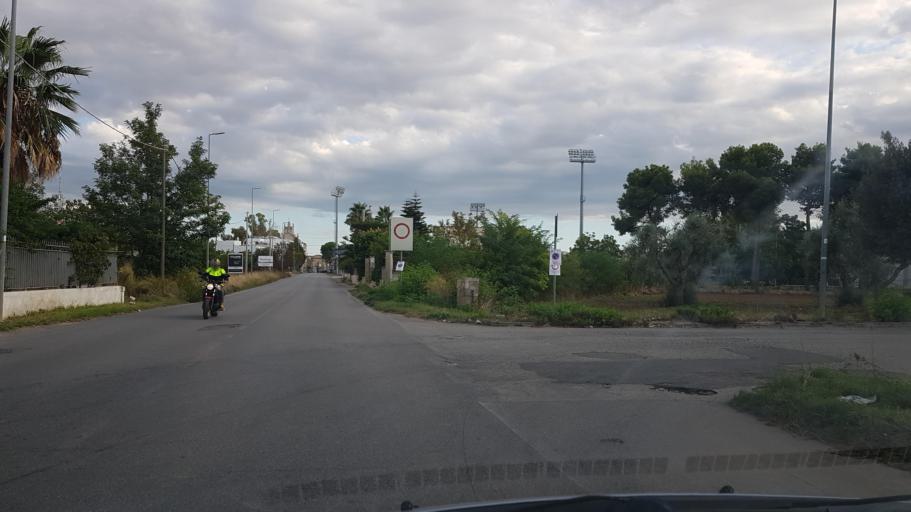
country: IT
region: Apulia
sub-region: Provincia di Brindisi
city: Francavilla Fontana
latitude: 40.5374
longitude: 17.5770
